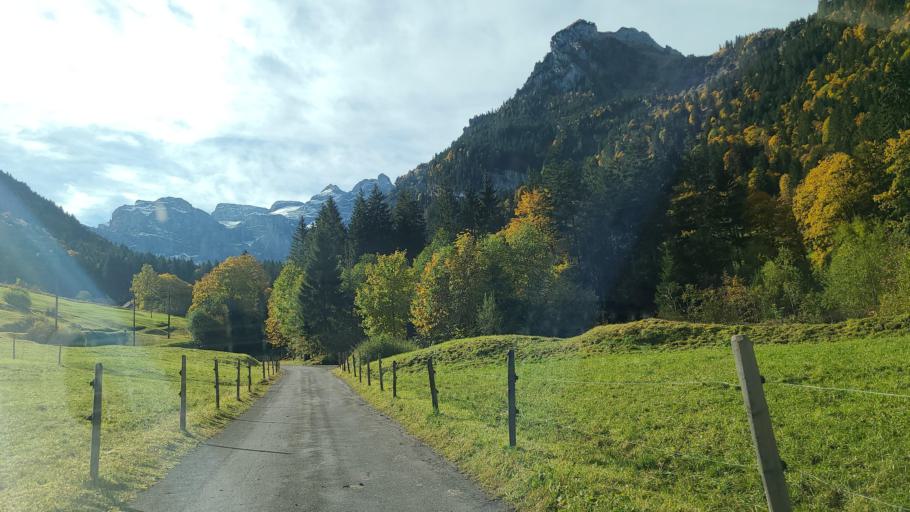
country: CH
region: Nidwalden
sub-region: Nidwalden
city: Emmetten
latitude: 46.9006
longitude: 8.5223
